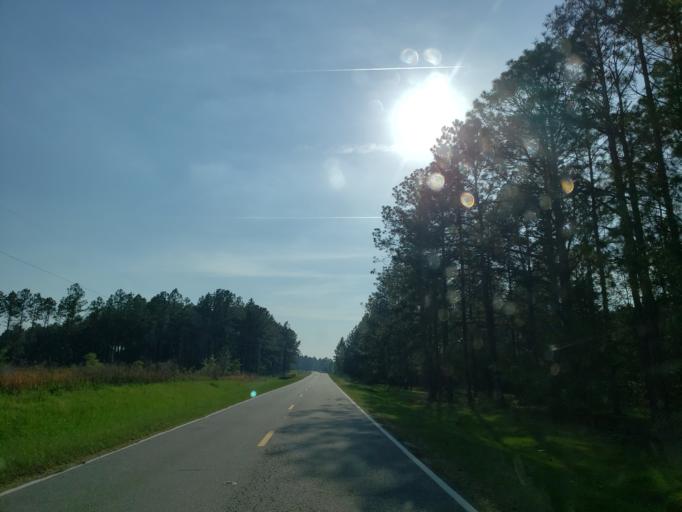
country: US
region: Georgia
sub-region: Tift County
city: Tifton
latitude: 31.5539
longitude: -83.5230
